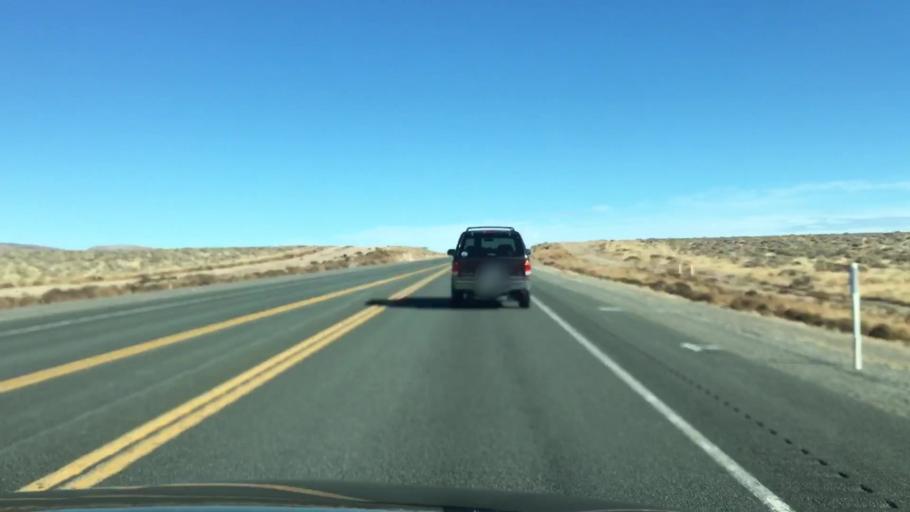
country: US
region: Nevada
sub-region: Lyon County
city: Stagecoach
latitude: 39.3694
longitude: -119.3526
